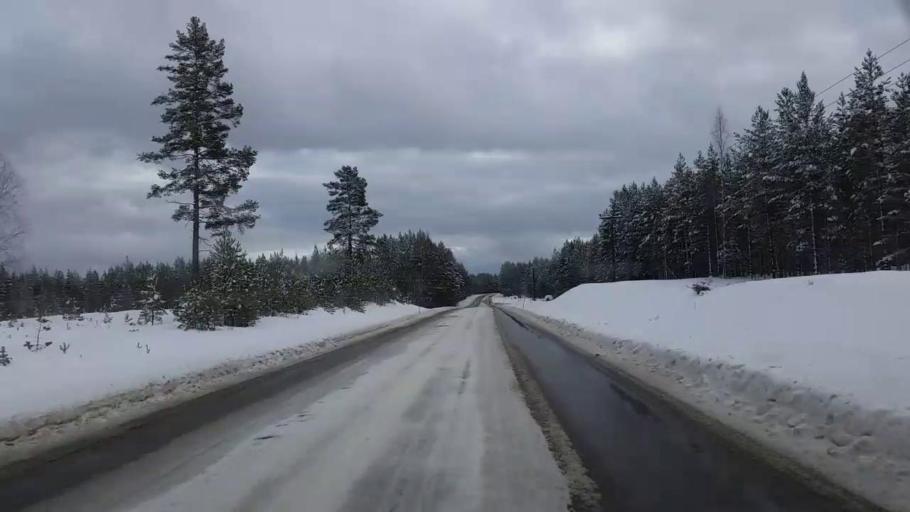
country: SE
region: Vaesternorrland
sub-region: Ange Kommun
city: Ange
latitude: 62.0941
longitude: 15.0851
